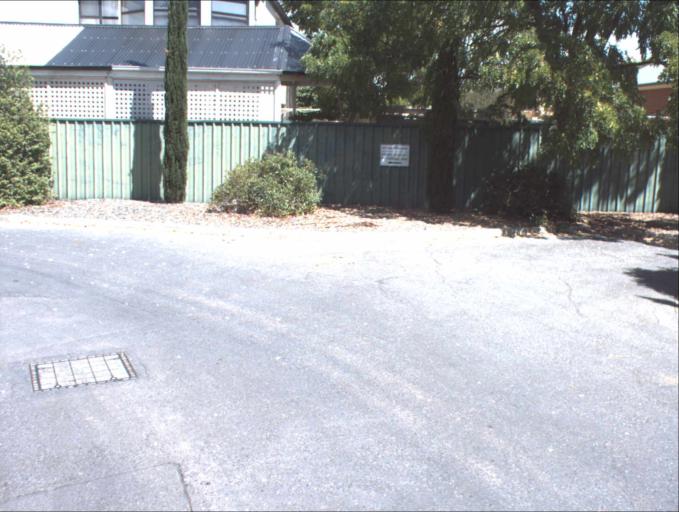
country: AU
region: South Australia
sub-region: Port Adelaide Enfield
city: Gilles Plains
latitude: -34.8534
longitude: 138.6401
